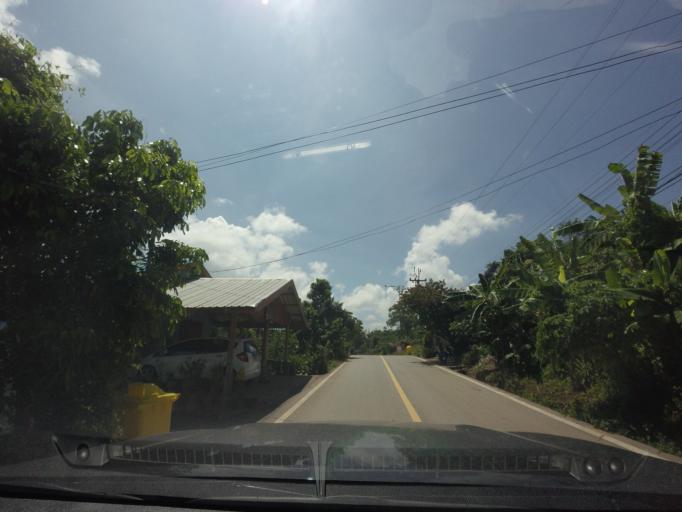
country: TH
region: Phetchabun
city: Khao Kho
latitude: 16.7796
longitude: 101.0474
